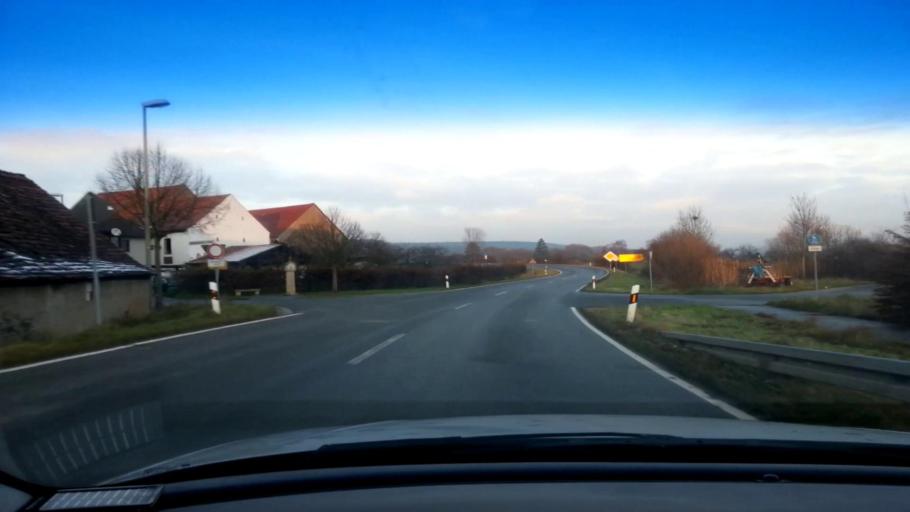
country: DE
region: Bavaria
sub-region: Upper Franconia
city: Frensdorf
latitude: 49.7914
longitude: 10.8874
